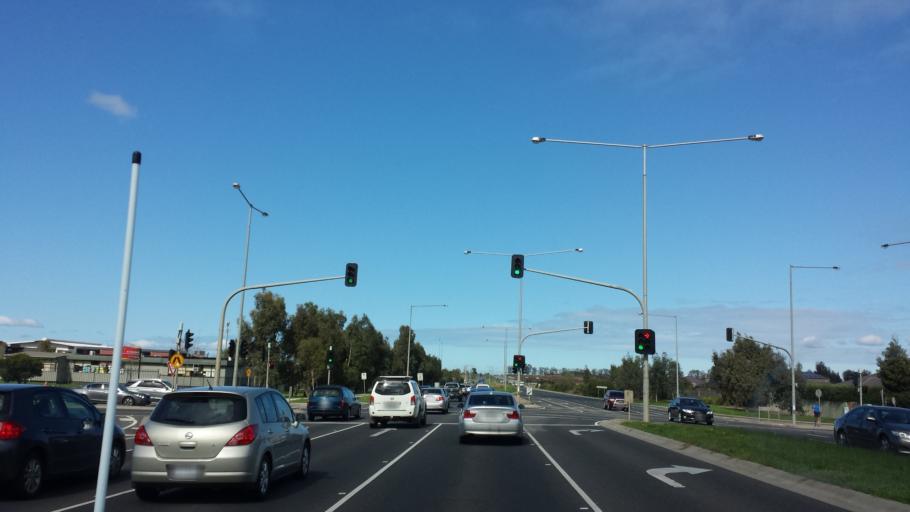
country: AU
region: Victoria
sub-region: Casey
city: Berwick
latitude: -38.0680
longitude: 145.3368
